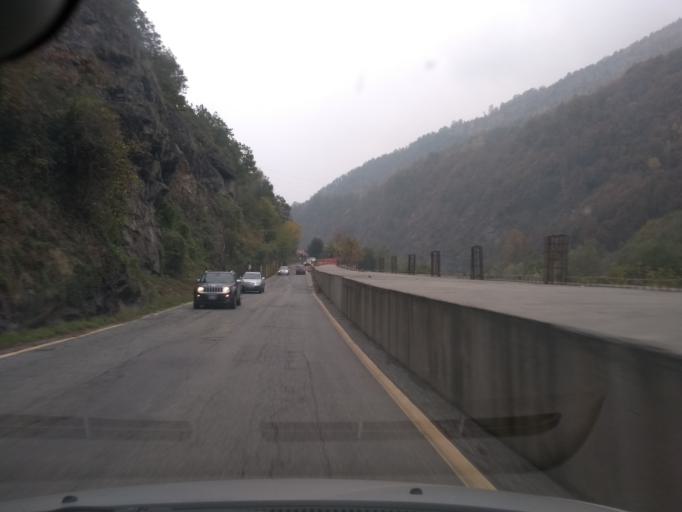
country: IT
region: Piedmont
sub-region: Provincia di Torino
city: Pessinetto
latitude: 45.2873
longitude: 7.4105
